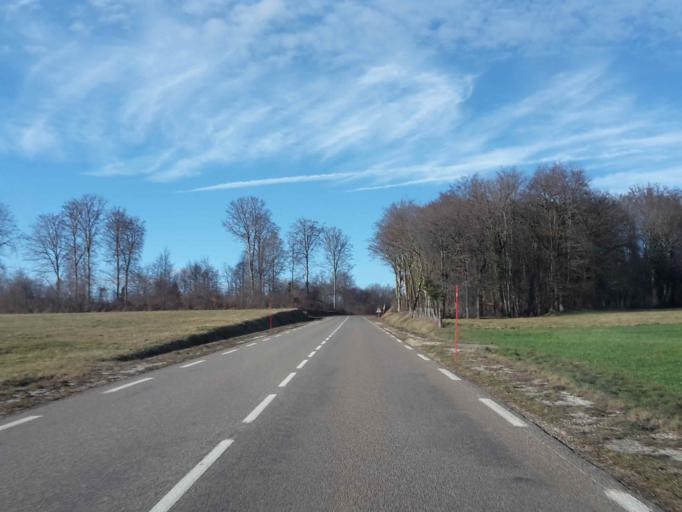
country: FR
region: Franche-Comte
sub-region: Departement du Doubs
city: Vercel-Villedieu-le-Camp
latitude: 47.1991
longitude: 6.3955
